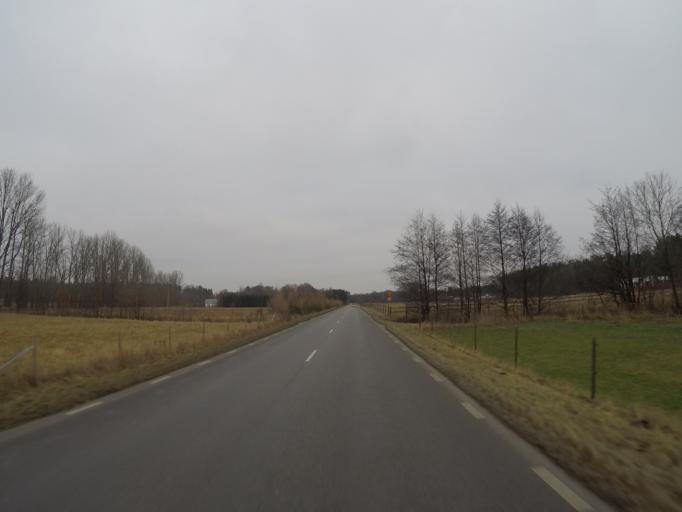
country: SE
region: Skane
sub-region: Hoors Kommun
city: Loberod
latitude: 55.7299
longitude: 13.3819
